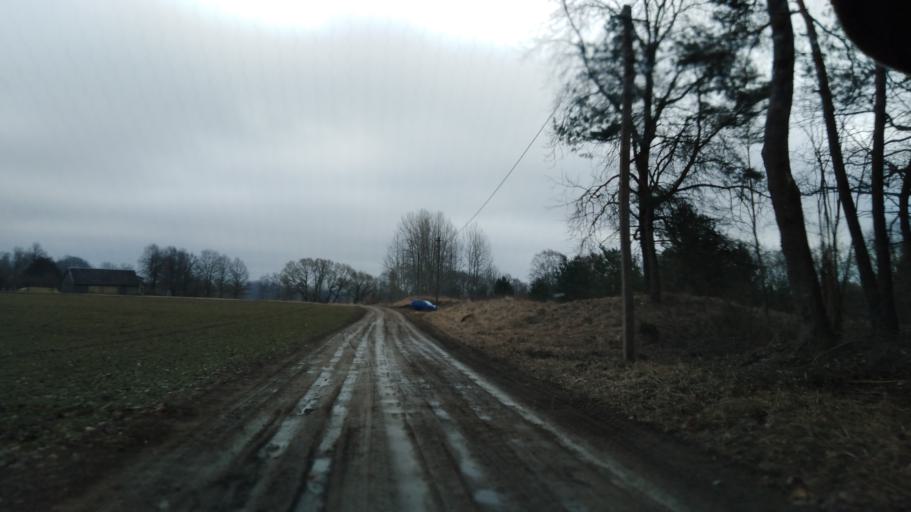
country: LV
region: Kuldigas Rajons
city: Kuldiga
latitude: 56.9847
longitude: 21.9622
